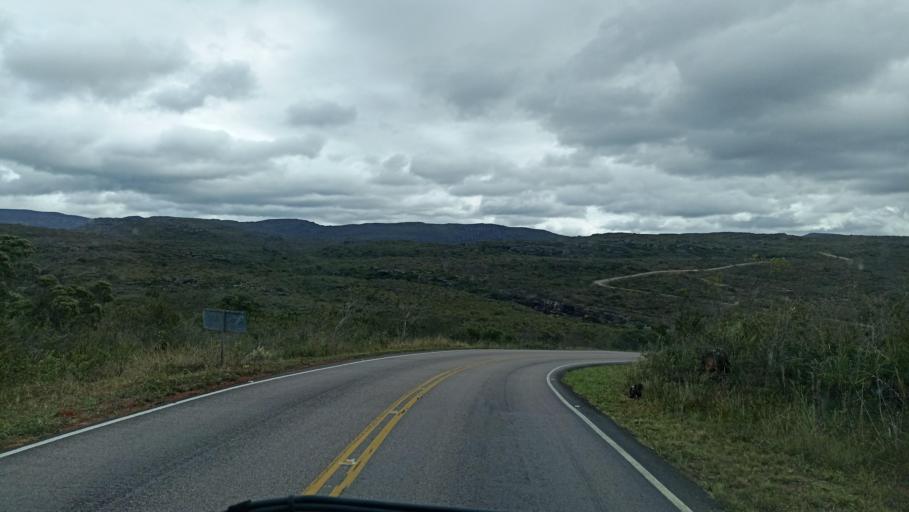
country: BR
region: Bahia
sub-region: Andarai
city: Vera Cruz
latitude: -12.9918
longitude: -41.3454
